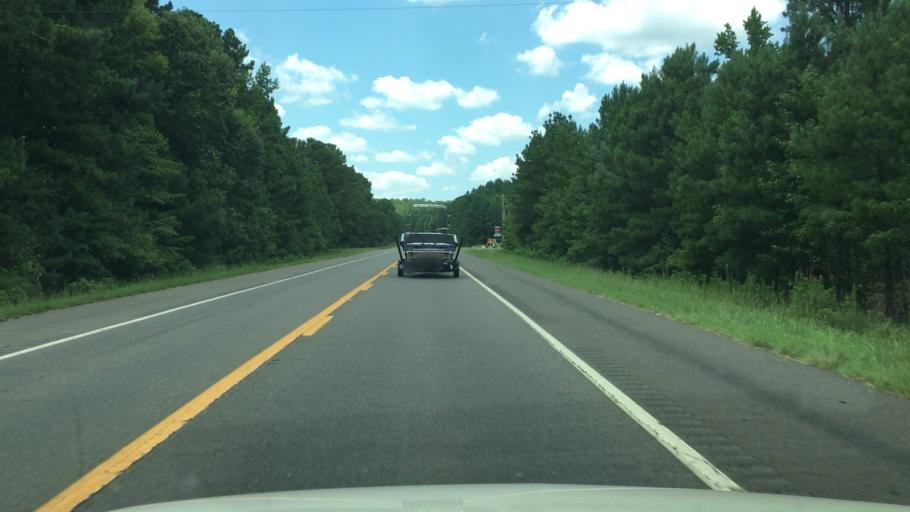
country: US
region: Arkansas
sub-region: Clark County
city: Arkadelphia
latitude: 34.2040
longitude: -93.0785
